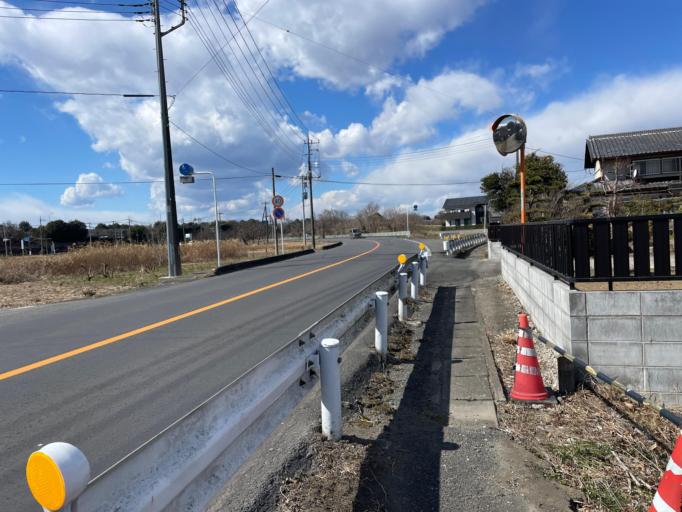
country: JP
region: Saitama
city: Sakado
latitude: 36.0164
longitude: 139.3863
